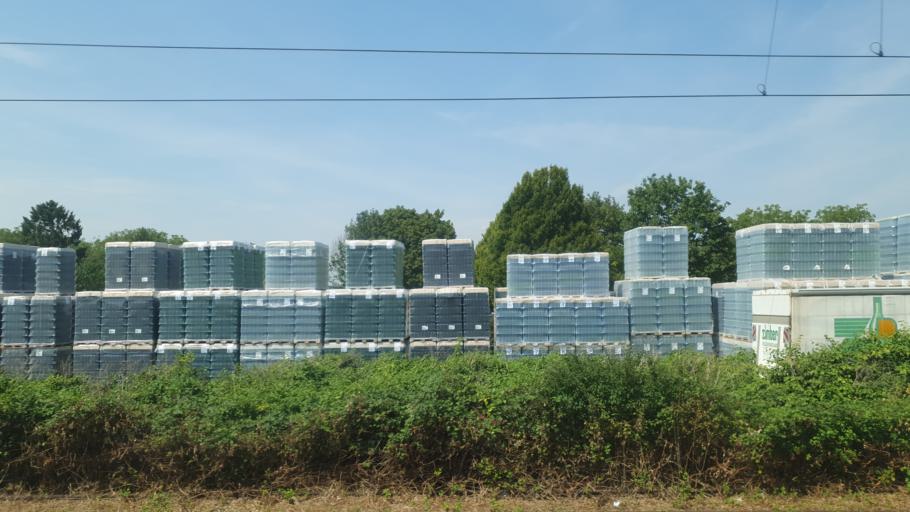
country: DE
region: Baden-Wuerttemberg
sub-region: Freiburg Region
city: Mullheim
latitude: 47.8128
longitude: 7.6013
